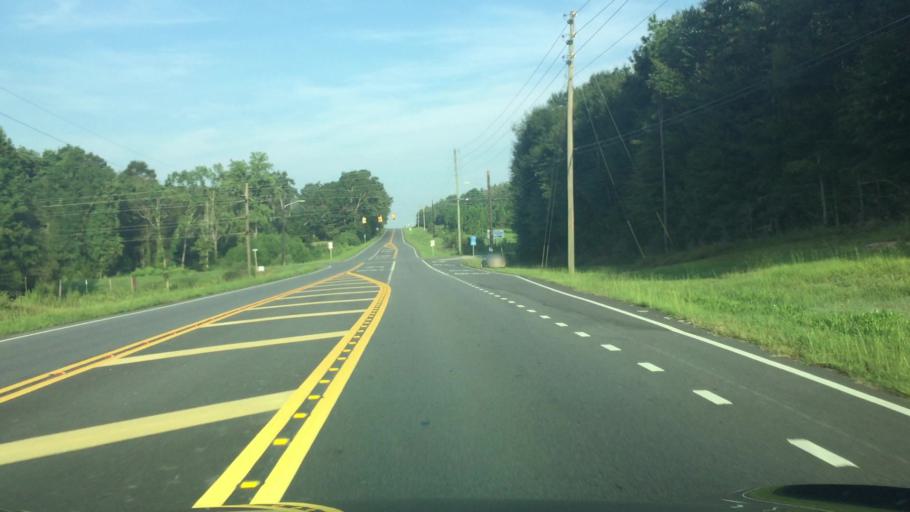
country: US
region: Alabama
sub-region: Covington County
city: Andalusia
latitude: 31.2781
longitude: -86.4965
